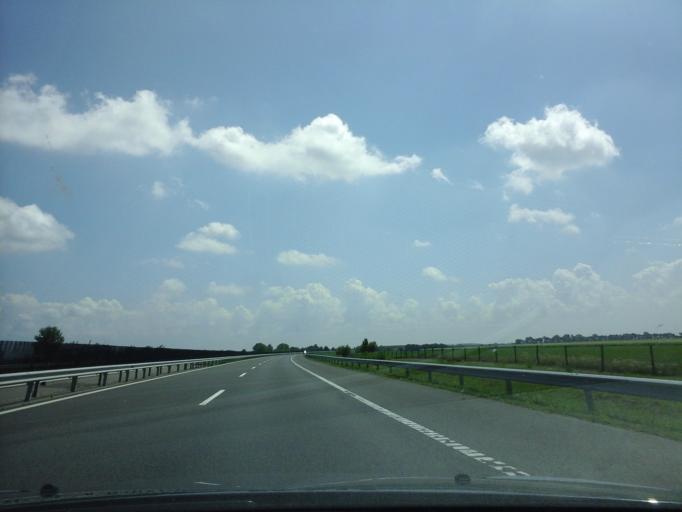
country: HU
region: Hajdu-Bihar
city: Hajduboszormeny
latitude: 47.7202
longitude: 21.4178
